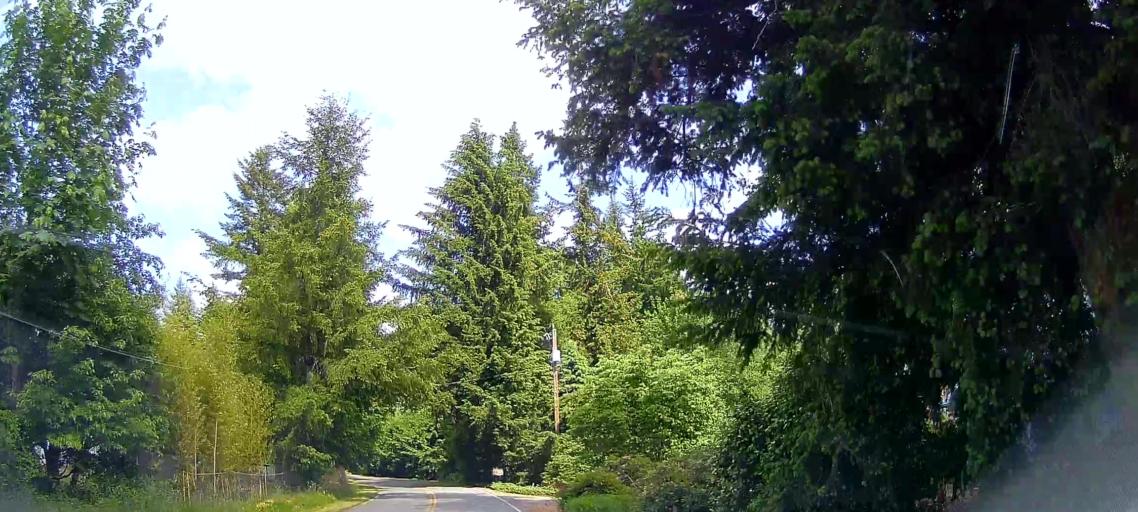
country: US
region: Washington
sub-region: Whatcom County
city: Sudden Valley
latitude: 48.6785
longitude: -122.1869
